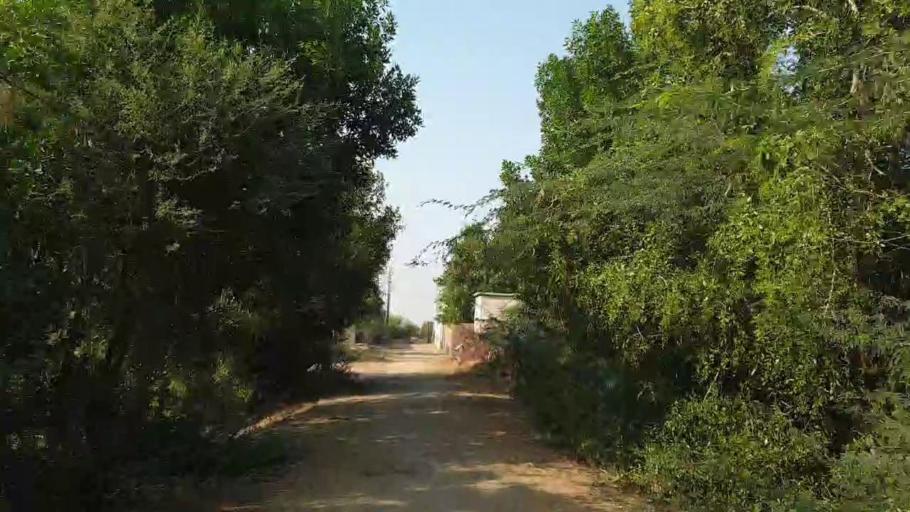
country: PK
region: Sindh
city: Bulri
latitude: 24.9928
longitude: 68.3725
